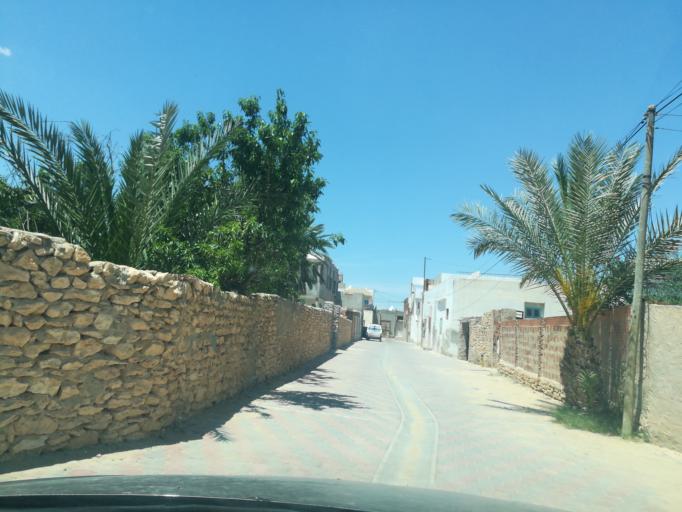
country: TN
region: Safaqis
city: Al Qarmadah
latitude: 34.8146
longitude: 10.7518
